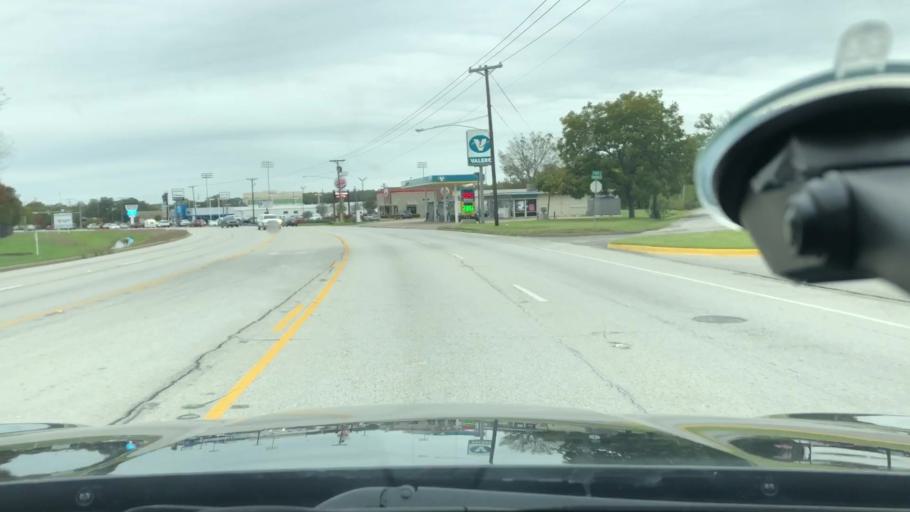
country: US
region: Texas
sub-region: Kaufman County
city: Terrell
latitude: 32.7387
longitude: -96.2904
